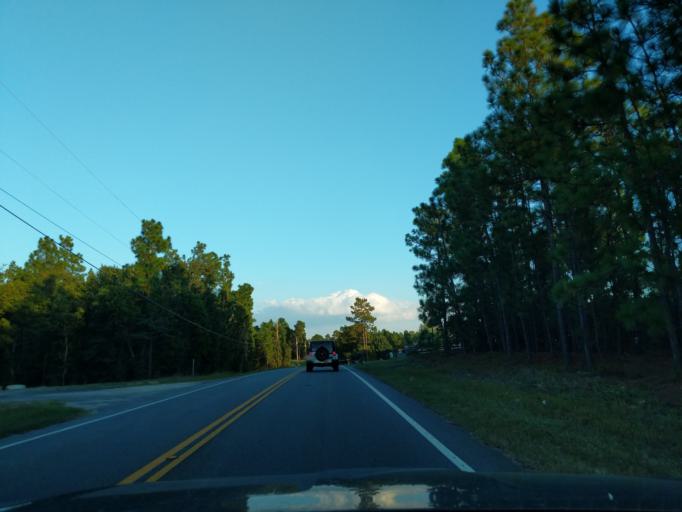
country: US
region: South Carolina
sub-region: Aiken County
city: Burnettown
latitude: 33.5383
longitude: -81.8670
